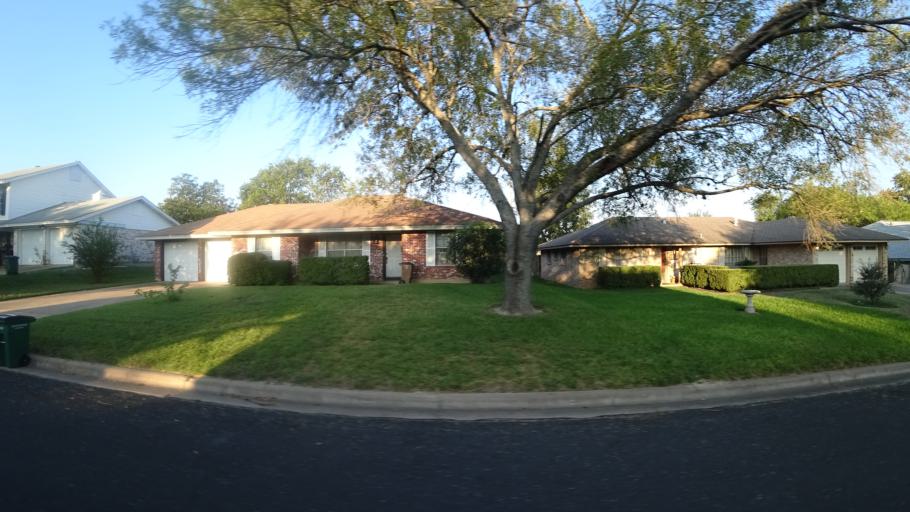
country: US
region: Texas
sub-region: Travis County
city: Austin
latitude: 30.3284
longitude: -97.6874
